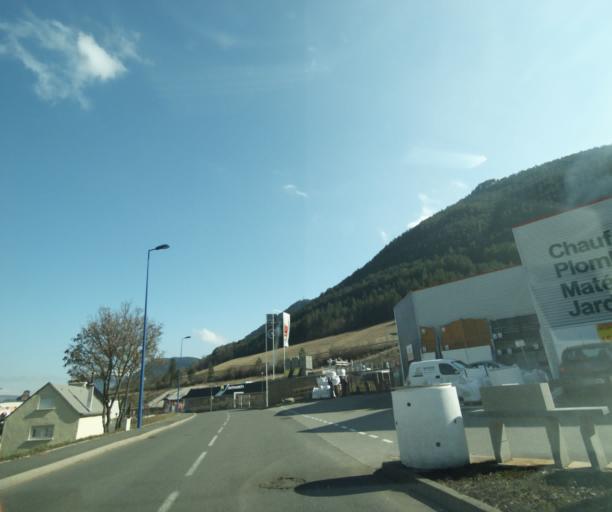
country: FR
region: Languedoc-Roussillon
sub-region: Departement de la Lozere
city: Mende
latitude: 44.5149
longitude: 3.4770
